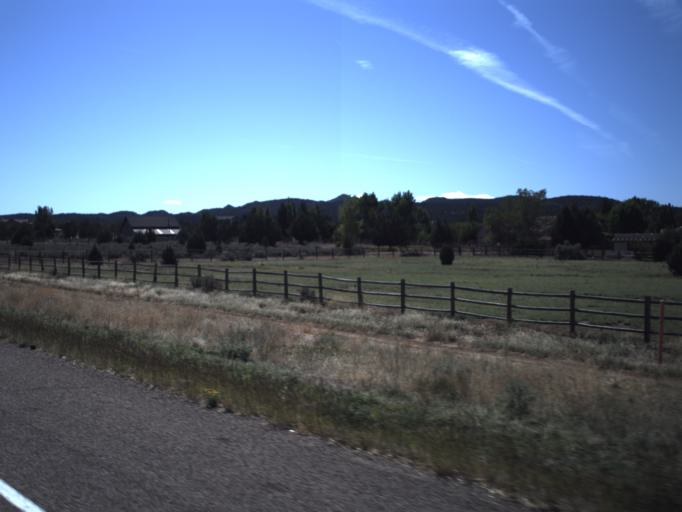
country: US
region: Utah
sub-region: Washington County
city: Ivins
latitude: 37.3091
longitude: -113.6732
